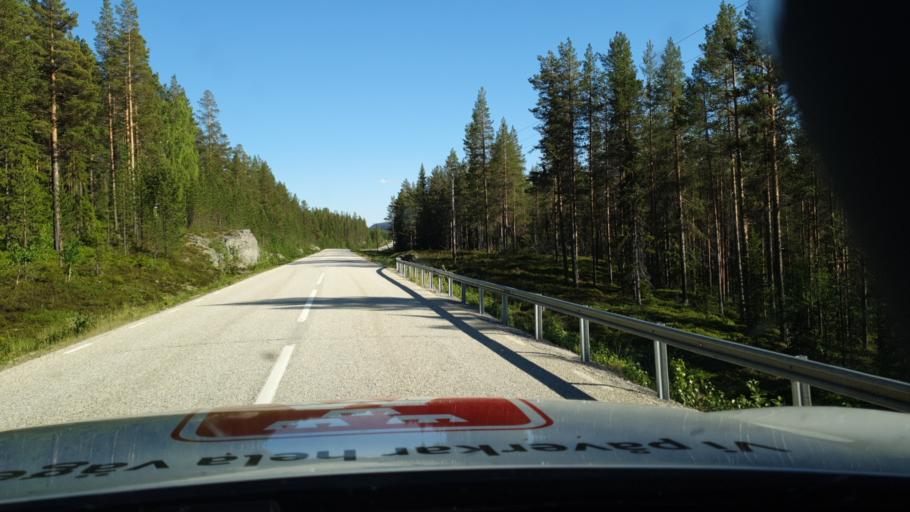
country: SE
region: Jaemtland
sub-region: Are Kommun
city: Jarpen
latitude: 62.7831
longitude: 13.6969
